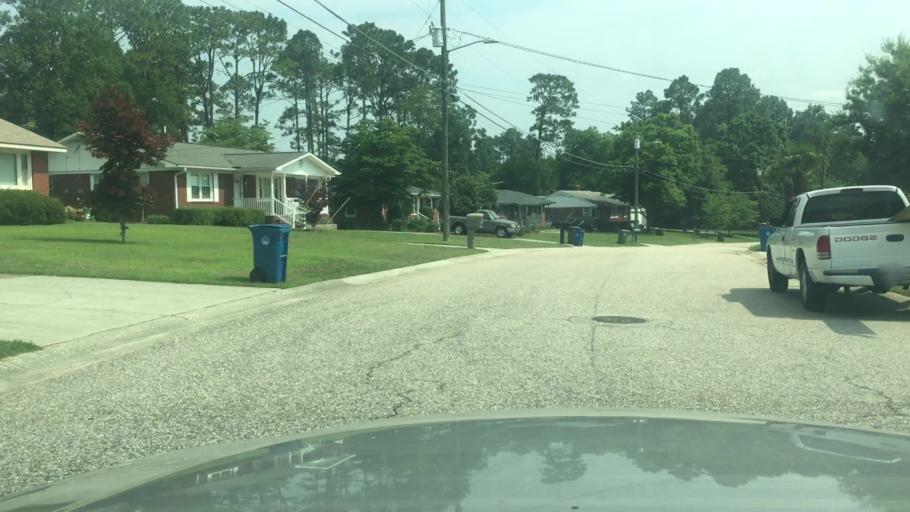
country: US
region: North Carolina
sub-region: Cumberland County
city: Hope Mills
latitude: 35.0307
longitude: -78.9446
